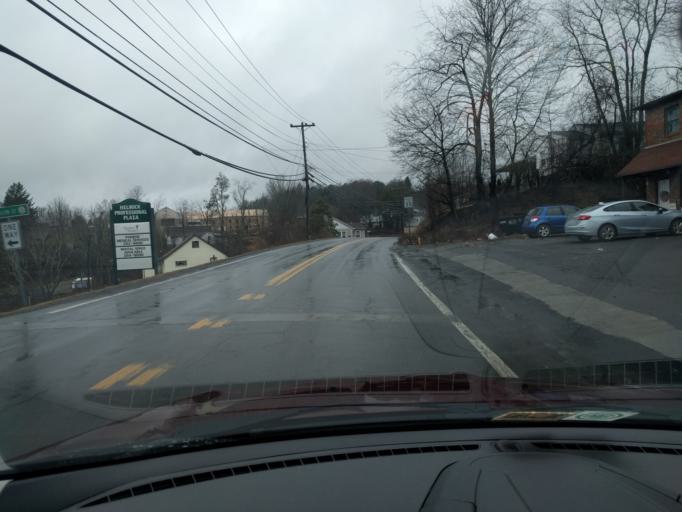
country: US
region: West Virginia
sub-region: Raleigh County
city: Beckley
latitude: 37.7920
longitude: -81.1800
